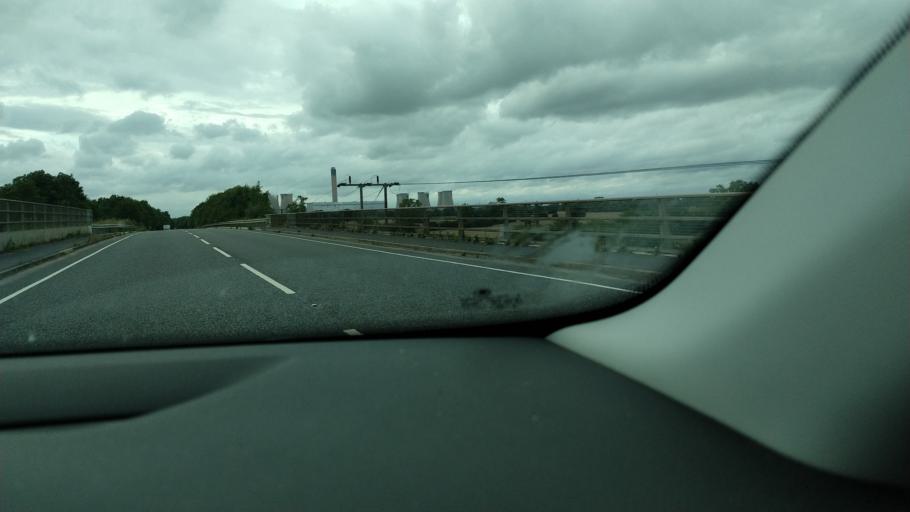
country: GB
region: England
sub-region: East Riding of Yorkshire
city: Rawcliffe
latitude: 53.7143
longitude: -0.9584
